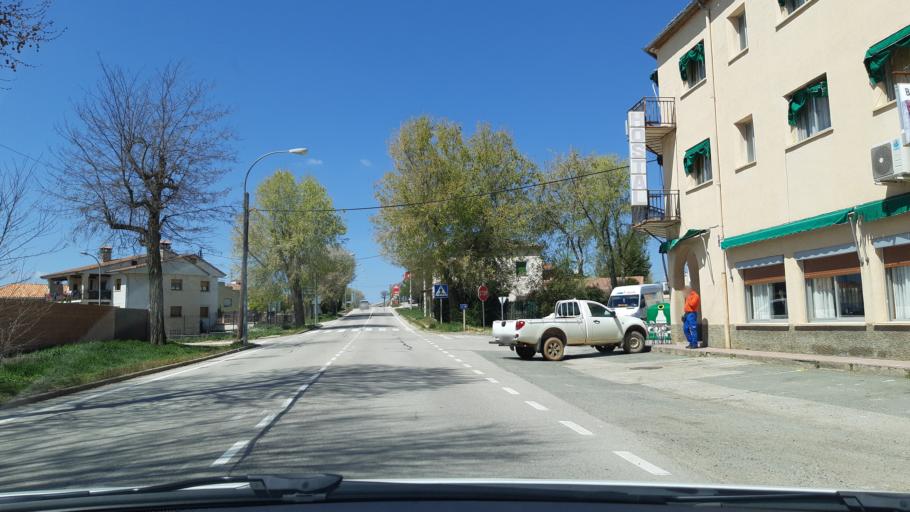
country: ES
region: Castille-La Mancha
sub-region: Provincia de Guadalajara
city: Cifuentes
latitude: 40.7842
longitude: -2.6267
